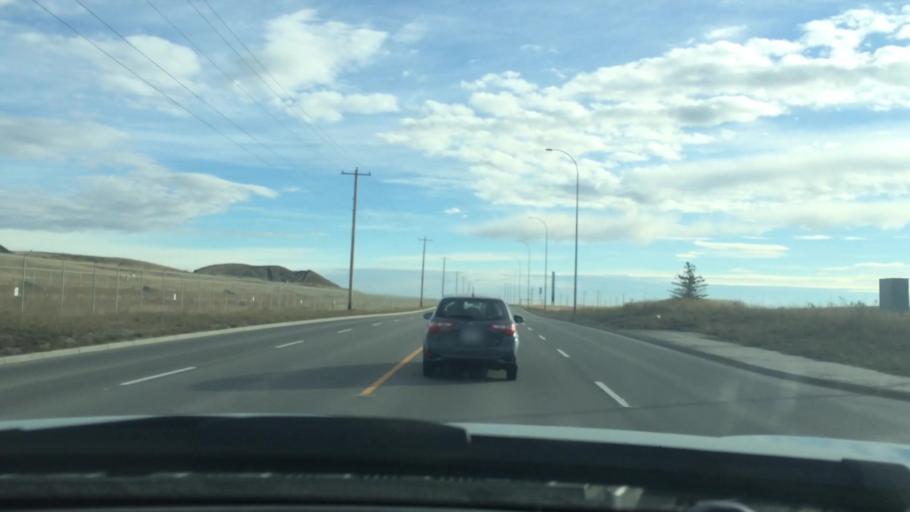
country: CA
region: Alberta
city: Calgary
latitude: 51.1541
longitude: -114.1741
